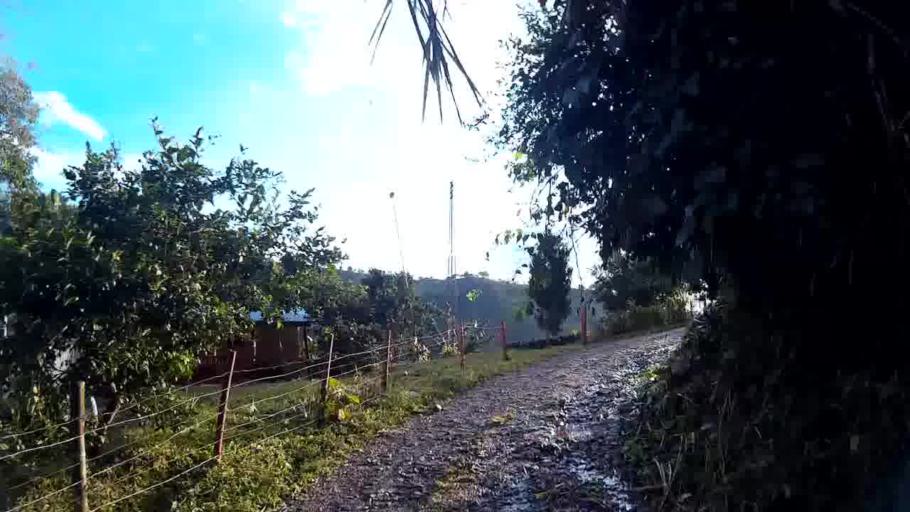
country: CO
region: Quindio
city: Filandia
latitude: 4.7153
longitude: -75.6862
